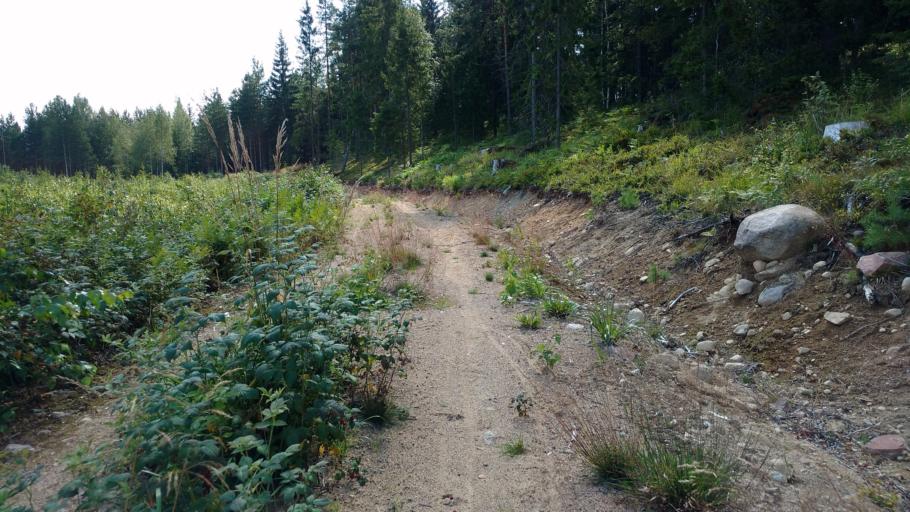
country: FI
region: Varsinais-Suomi
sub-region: Salo
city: Pertteli
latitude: 60.3939
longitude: 23.2317
